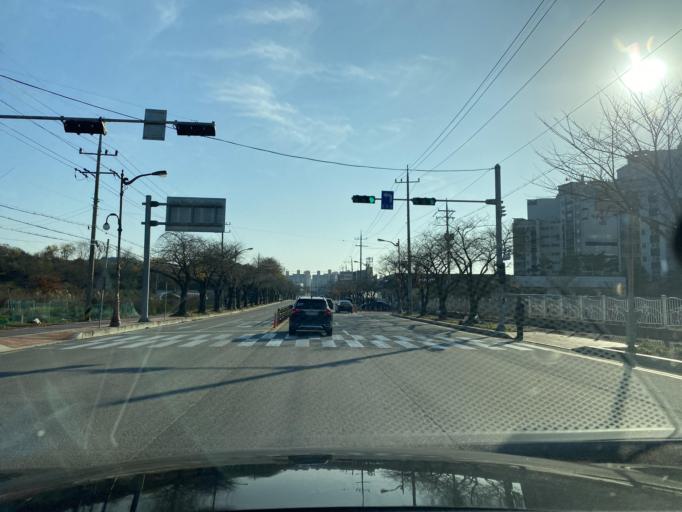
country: KR
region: Chungcheongnam-do
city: Yesan
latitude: 36.6968
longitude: 126.8372
